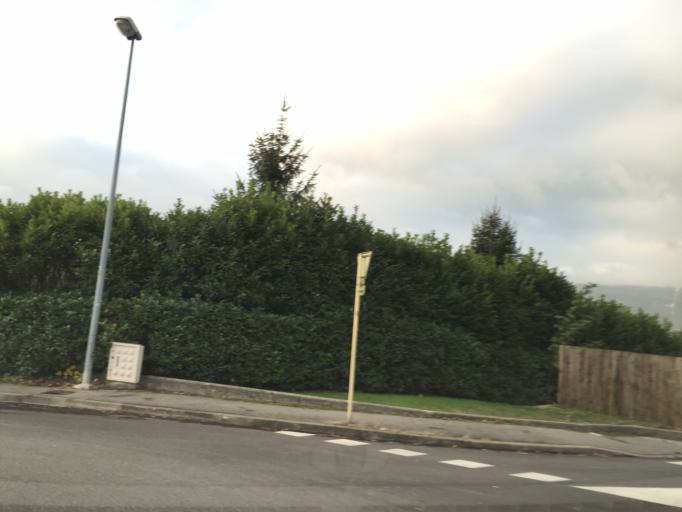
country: FR
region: Rhone-Alpes
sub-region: Departement de la Savoie
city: Sonnaz
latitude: 45.5976
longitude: 5.9056
